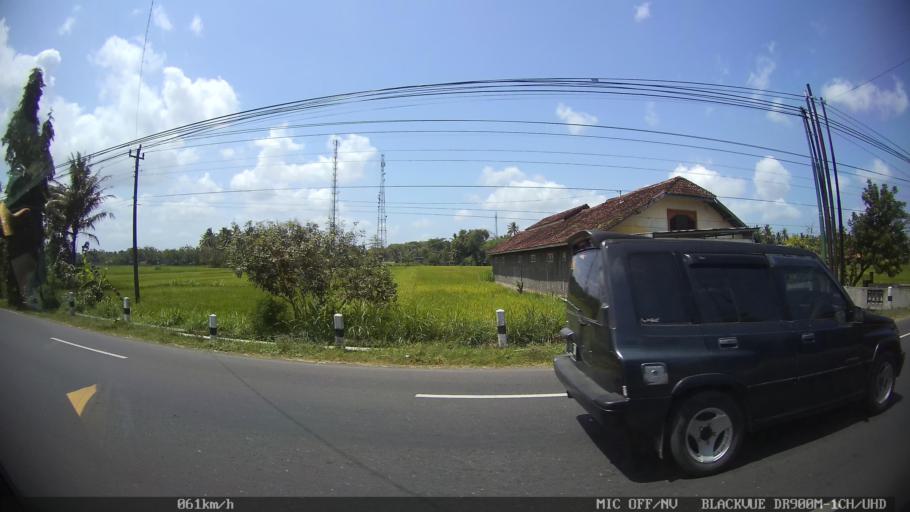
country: ID
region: Daerah Istimewa Yogyakarta
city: Pandak
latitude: -7.9158
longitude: 110.2864
